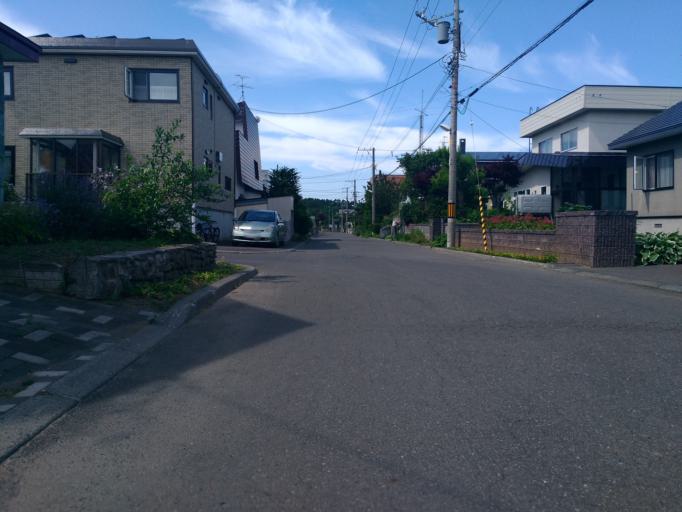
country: JP
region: Hokkaido
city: Ebetsu
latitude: 43.0785
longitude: 141.5006
